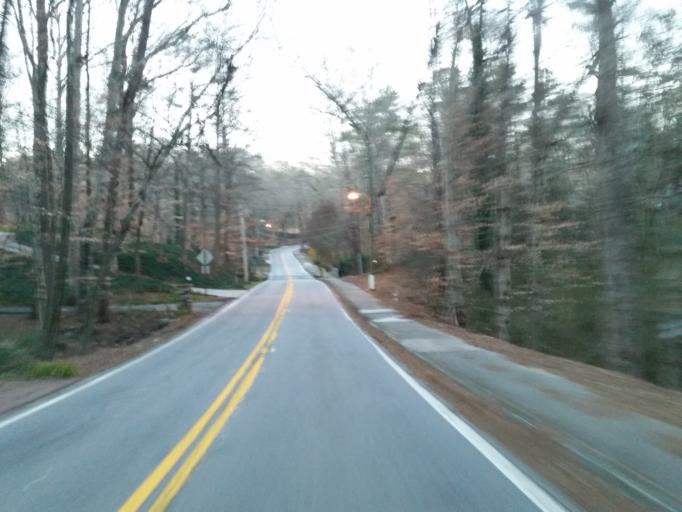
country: US
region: Georgia
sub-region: Cobb County
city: Vinings
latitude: 33.8452
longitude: -84.4701
